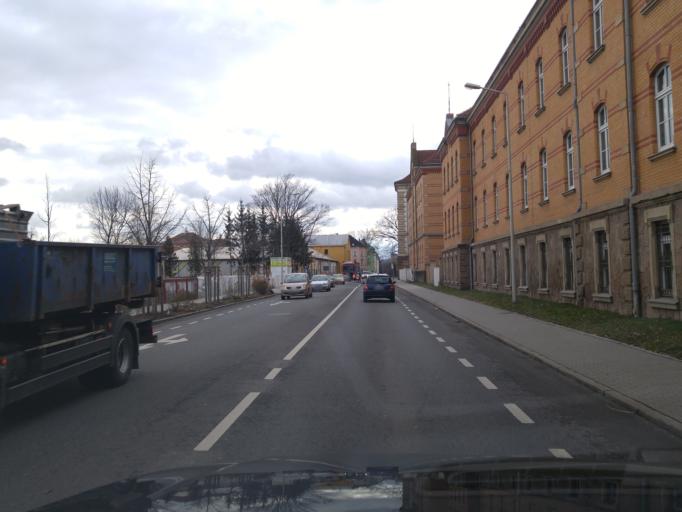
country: DE
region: Saxony
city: Weissenborn
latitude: 50.7240
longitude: 12.4757
